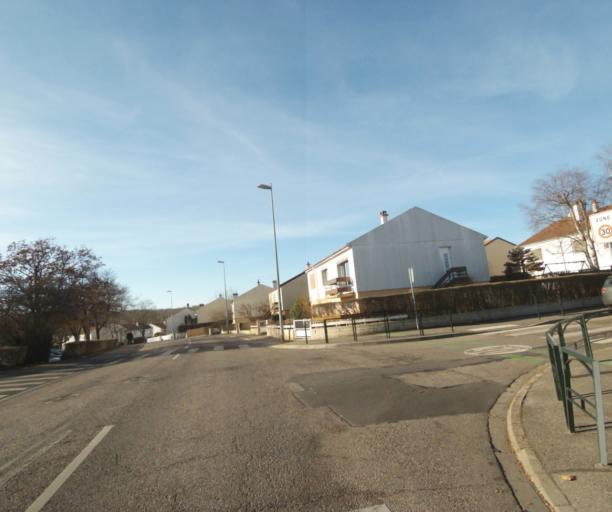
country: FR
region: Lorraine
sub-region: Departement de Meurthe-et-Moselle
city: Chavigny
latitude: 48.6587
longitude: 6.1113
